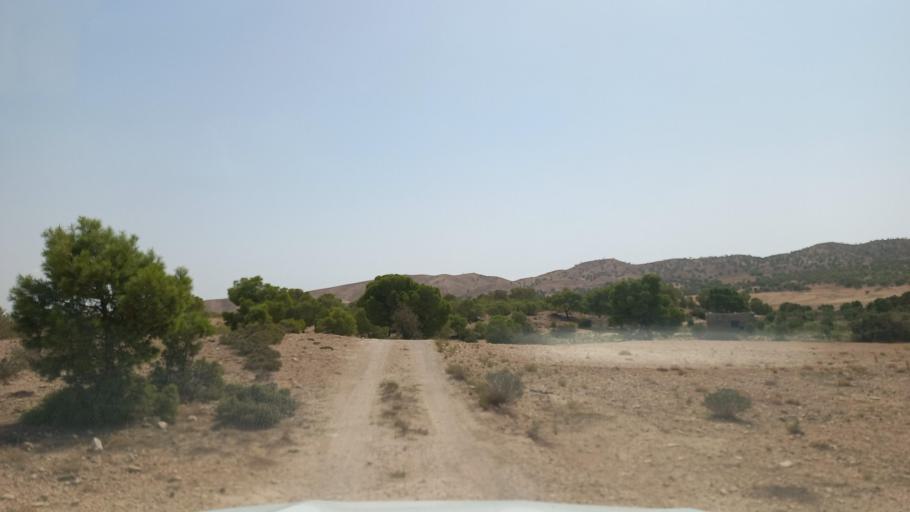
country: TN
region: Al Qasrayn
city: Sbiba
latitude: 35.3949
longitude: 8.9864
